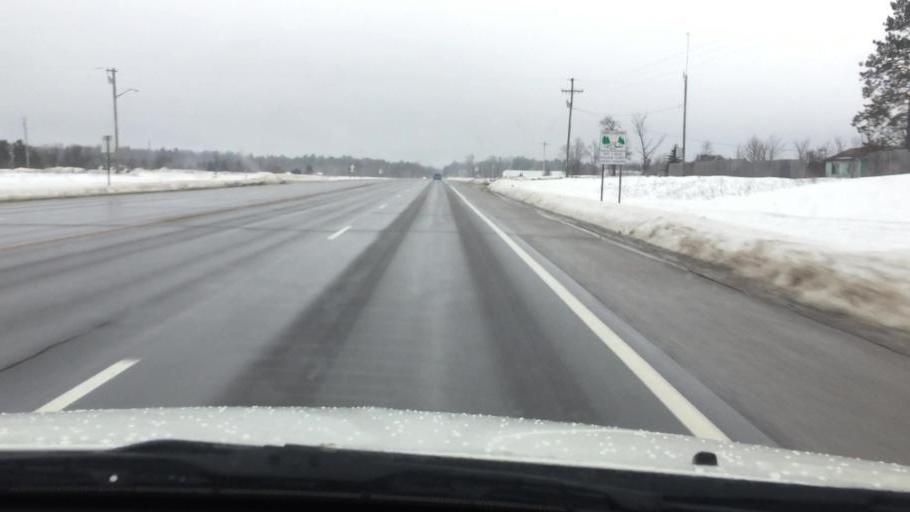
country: US
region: Michigan
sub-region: Kalkaska County
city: Kalkaska
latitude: 44.6741
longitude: -85.2360
